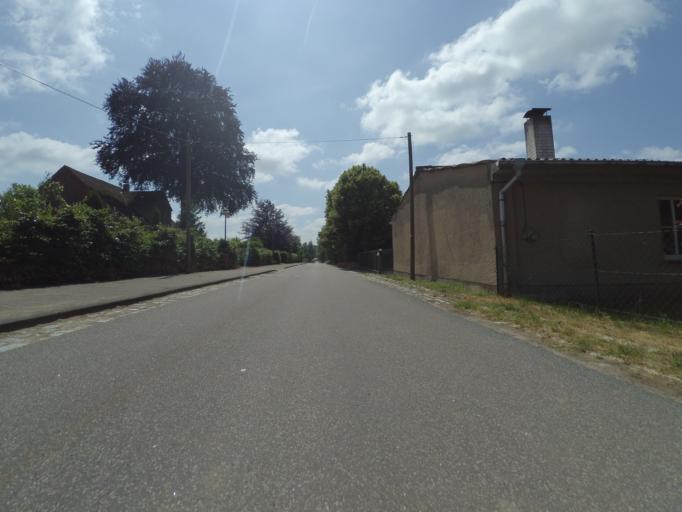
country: DE
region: Mecklenburg-Vorpommern
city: Neuburg
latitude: 53.4678
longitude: 11.9446
